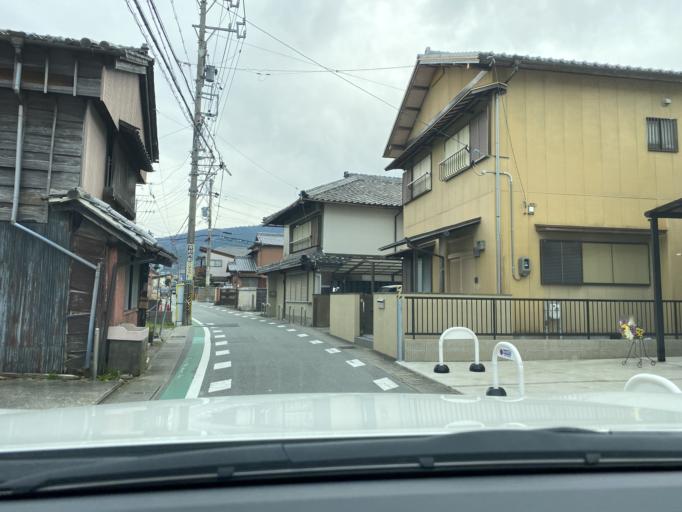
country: JP
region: Mie
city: Ise
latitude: 34.4769
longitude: 136.7204
